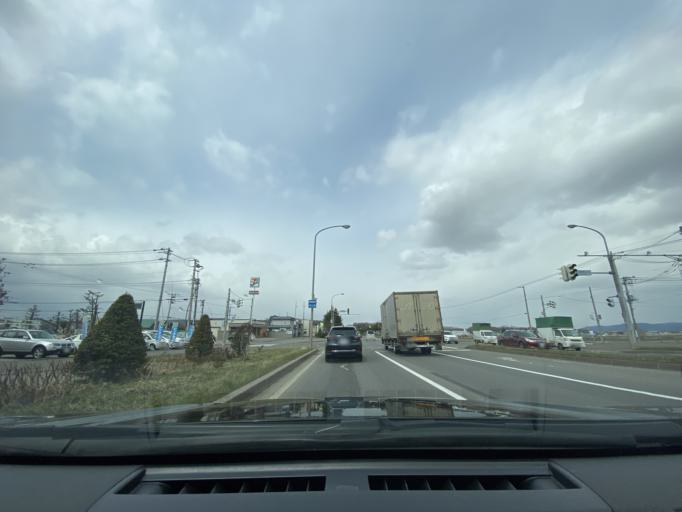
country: JP
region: Hokkaido
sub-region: Asahikawa-shi
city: Asahikawa
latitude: 43.8182
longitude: 142.3977
